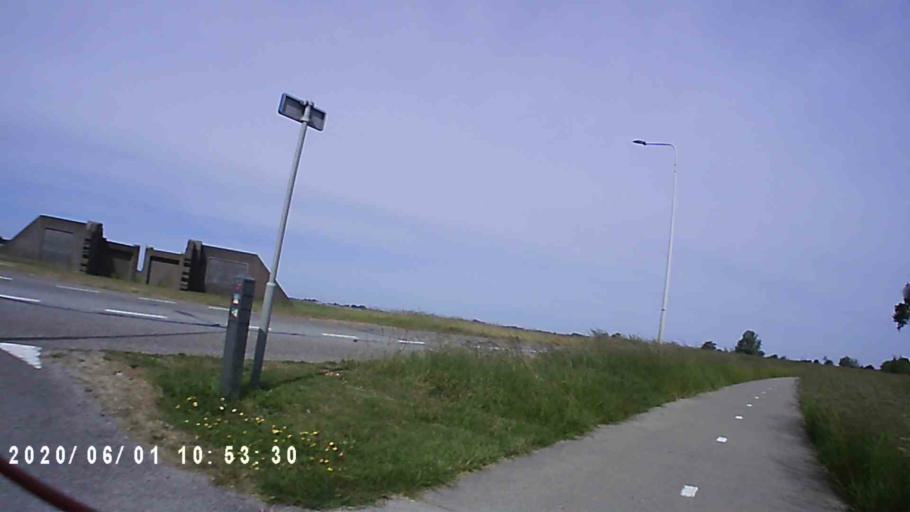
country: NL
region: Friesland
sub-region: Gemeente Franekeradeel
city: Franeker
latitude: 53.2018
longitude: 5.5134
